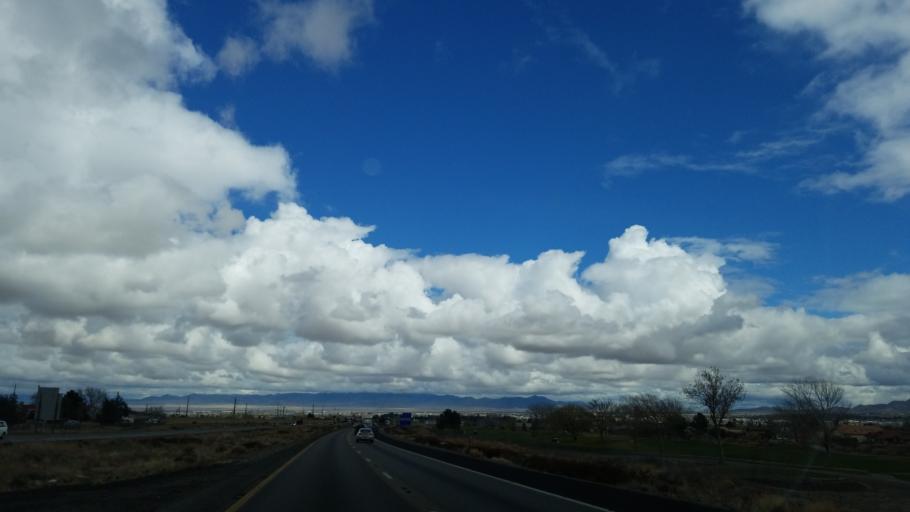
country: US
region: Arizona
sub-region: Mohave County
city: Kingman
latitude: 35.2130
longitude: -114.0498
